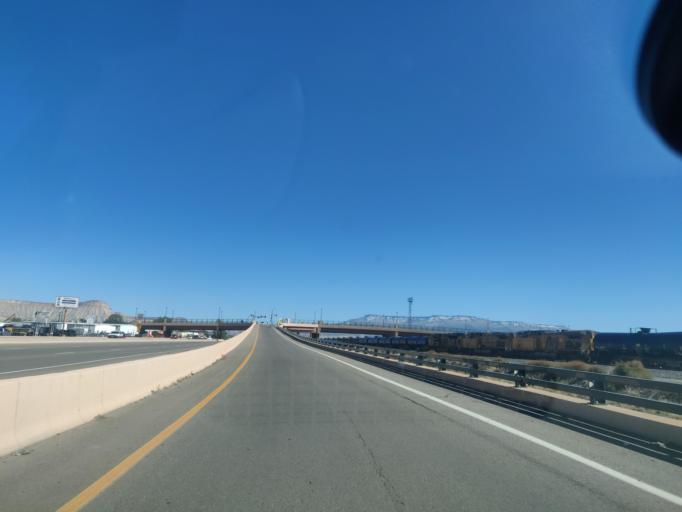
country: US
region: Colorado
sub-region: Mesa County
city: Fruitvale
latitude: 39.0716
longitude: -108.5188
